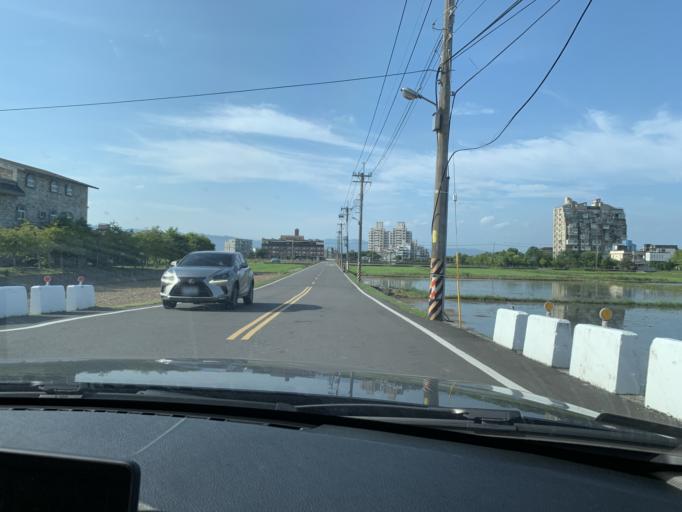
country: TW
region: Taiwan
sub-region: Yilan
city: Yilan
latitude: 24.6749
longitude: 121.8101
